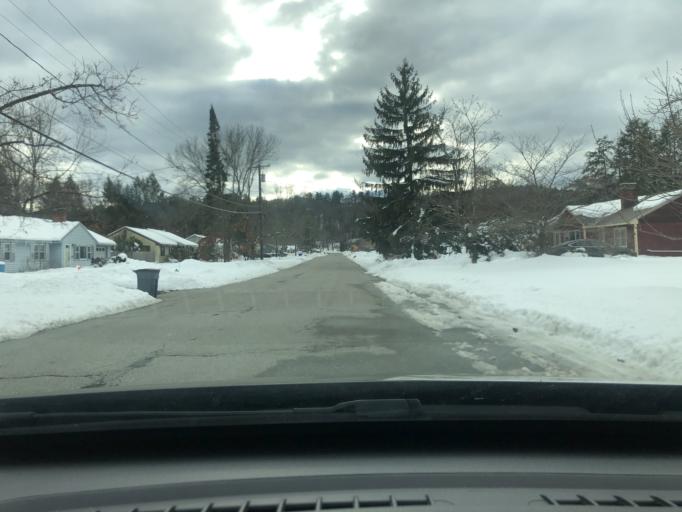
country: US
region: Massachusetts
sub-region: Middlesex County
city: Maynard
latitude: 42.4396
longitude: -71.4664
